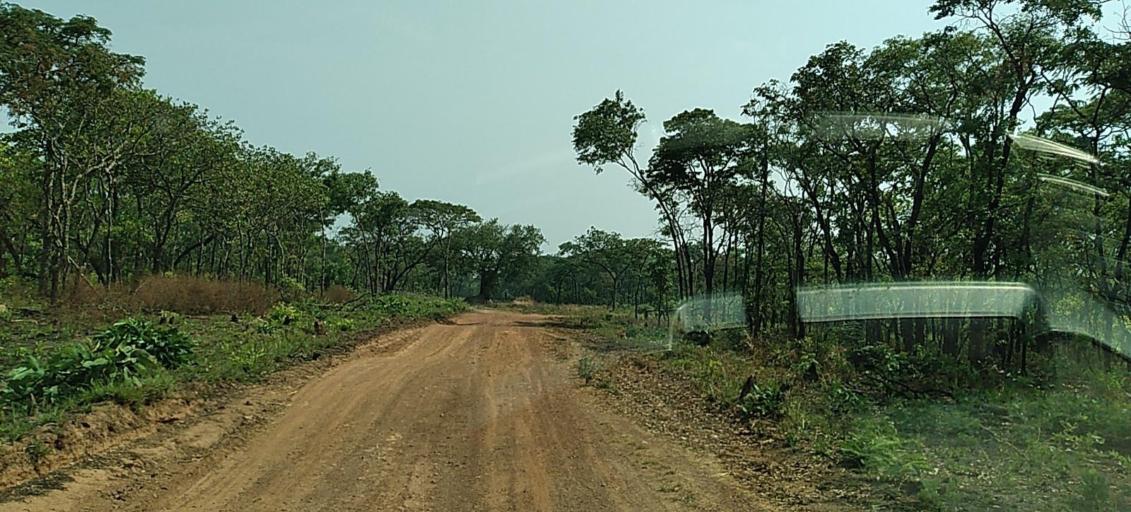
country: ZM
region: North-Western
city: Kansanshi
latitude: -12.0866
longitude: 26.8882
